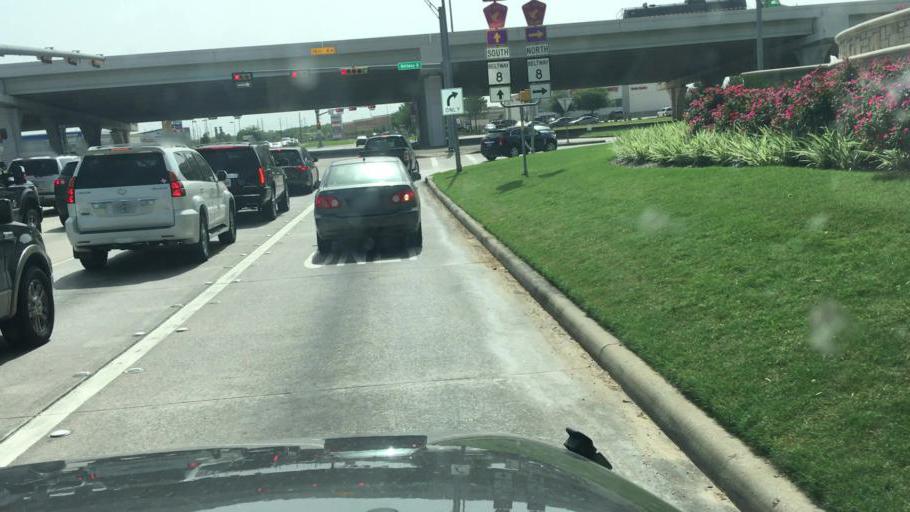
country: US
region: Texas
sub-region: Harris County
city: Atascocita
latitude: 29.9250
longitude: -95.1989
